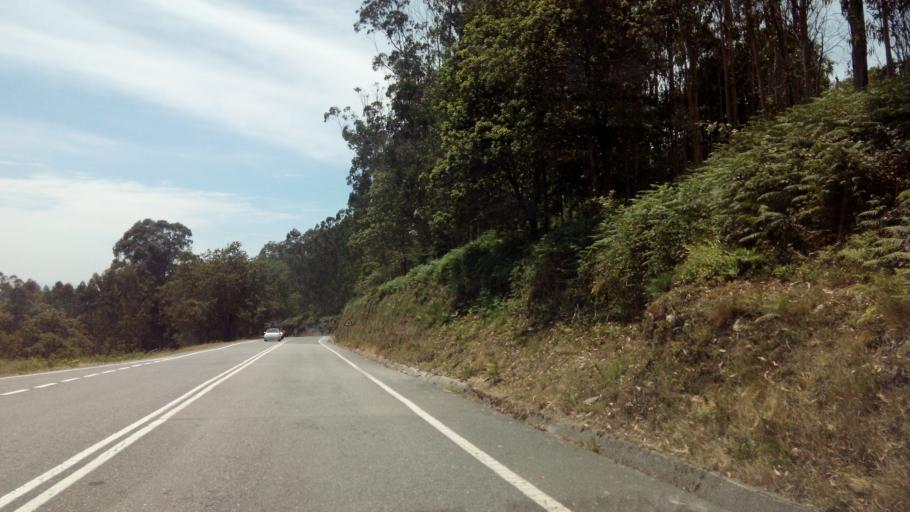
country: ES
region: Galicia
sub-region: Provincia de Pontevedra
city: Marin
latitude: 42.3313
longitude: -8.7171
